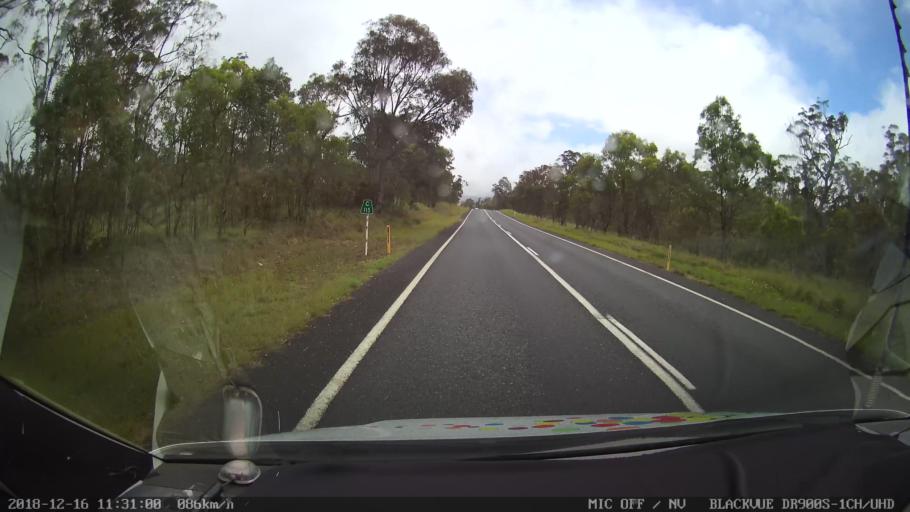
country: AU
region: New South Wales
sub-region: Tenterfield Municipality
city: Carrolls Creek
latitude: -29.0258
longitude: 152.1235
